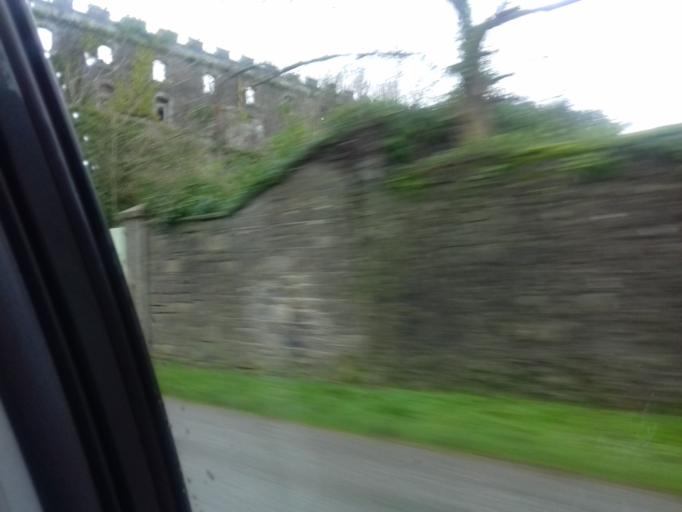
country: IE
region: Leinster
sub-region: County Carlow
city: Bagenalstown
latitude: 52.6480
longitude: -6.9885
